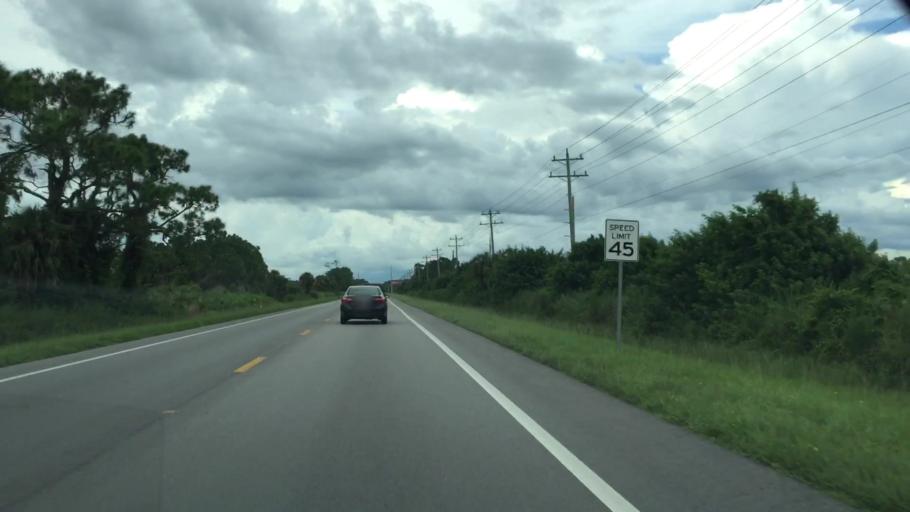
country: US
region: Florida
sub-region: Collier County
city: Immokalee
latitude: 26.3896
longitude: -81.4171
